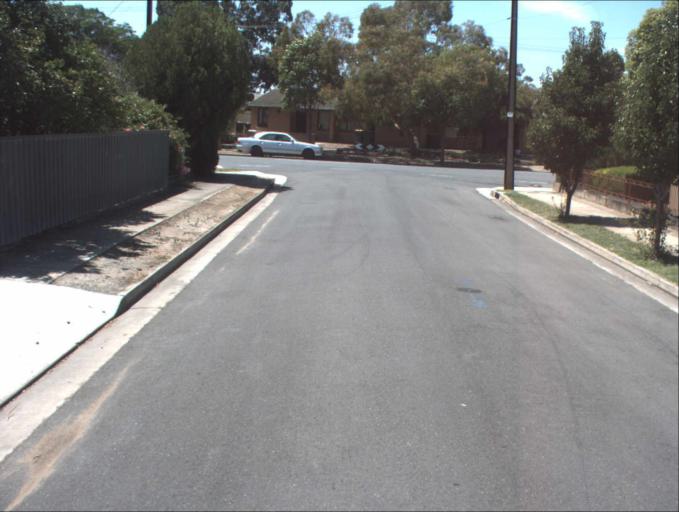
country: AU
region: South Australia
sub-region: Port Adelaide Enfield
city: Alberton
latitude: -34.8483
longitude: 138.5317
